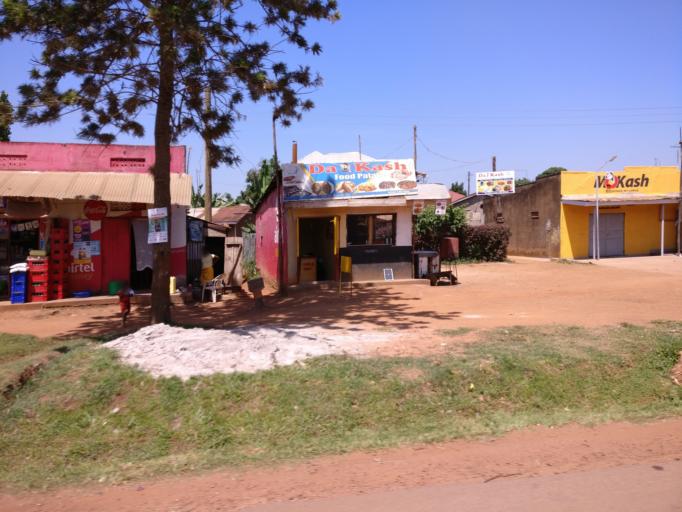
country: UG
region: Central Region
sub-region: Wakiso District
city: Entebbe
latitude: 0.1056
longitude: 32.5162
